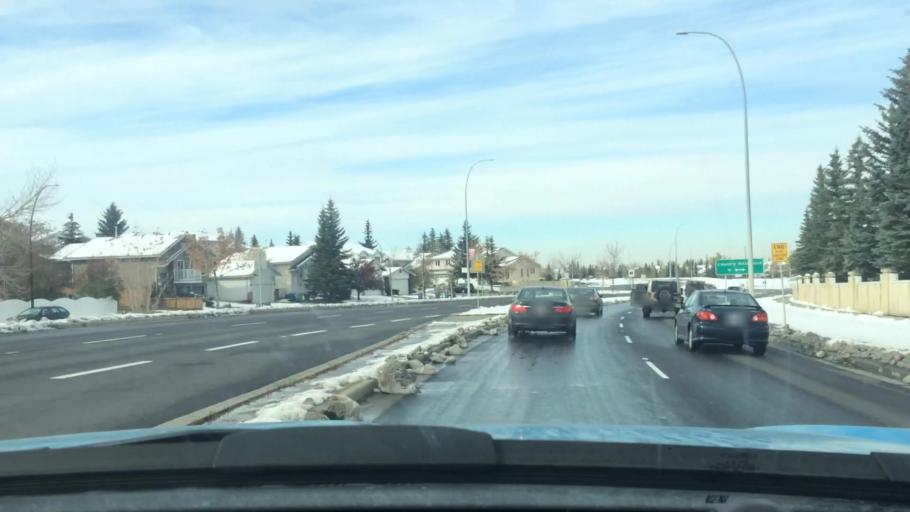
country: CA
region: Alberta
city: Calgary
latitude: 51.1409
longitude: -114.1089
